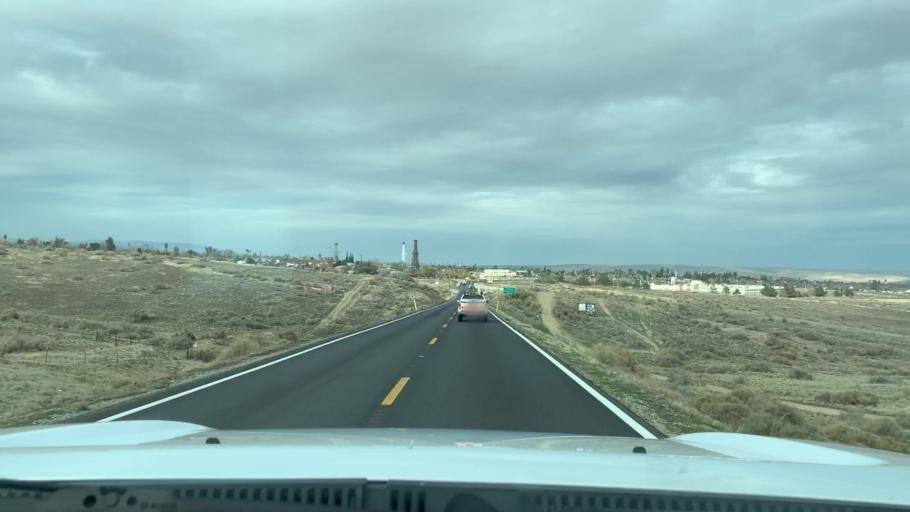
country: US
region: California
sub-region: Kern County
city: South Taft
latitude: 35.1286
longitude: -119.4426
